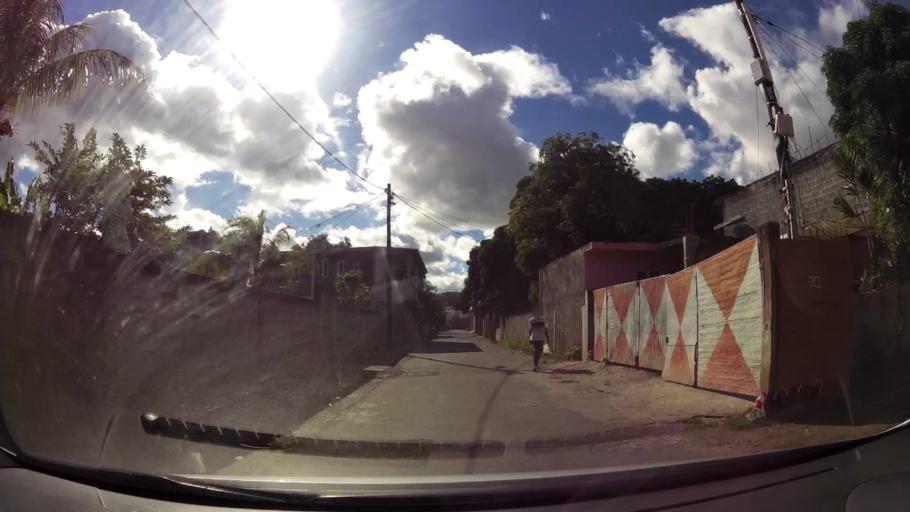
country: MU
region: Pamplemousses
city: Le Hochet
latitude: -20.1480
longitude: 57.5171
